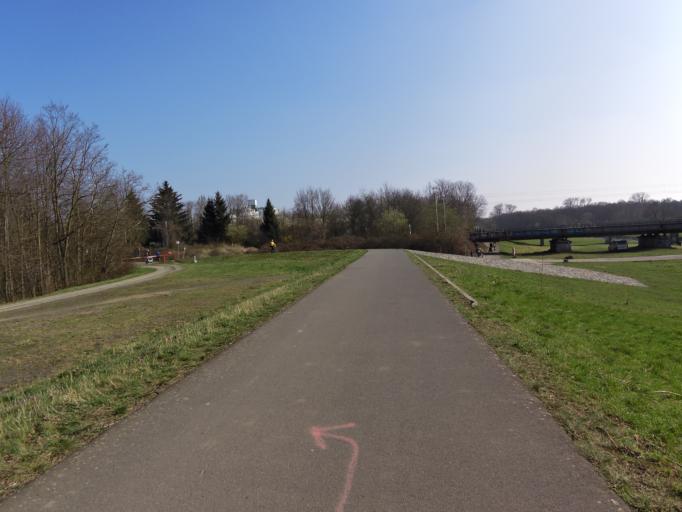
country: DE
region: Saxony
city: Leipzig
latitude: 51.3616
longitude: 12.3351
